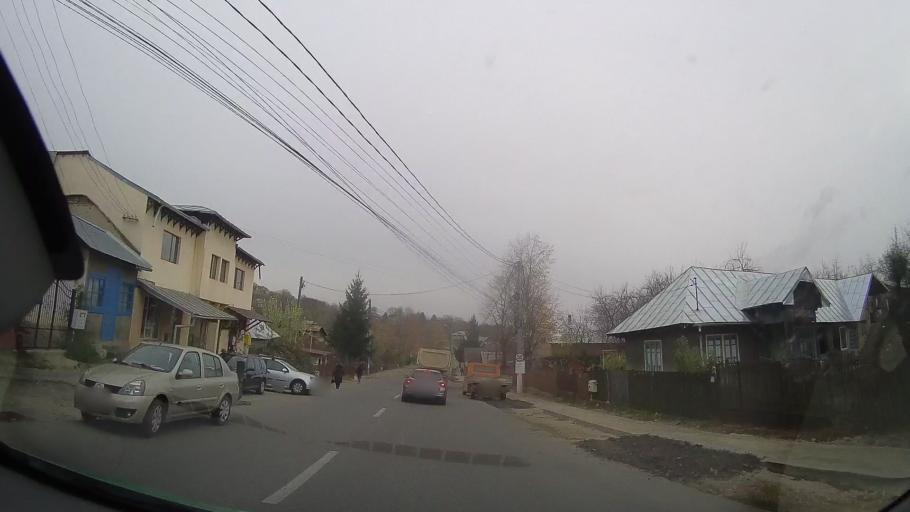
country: RO
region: Prahova
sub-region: Oras Baicoi
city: Tintea
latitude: 45.0342
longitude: 25.8997
